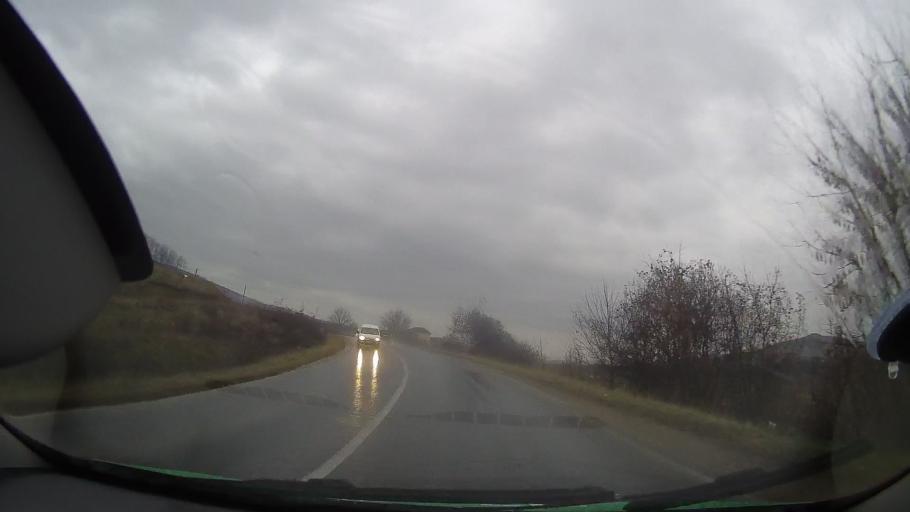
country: RO
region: Bihor
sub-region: Comuna Rabagani
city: Rabagani
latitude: 46.7558
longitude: 22.2056
